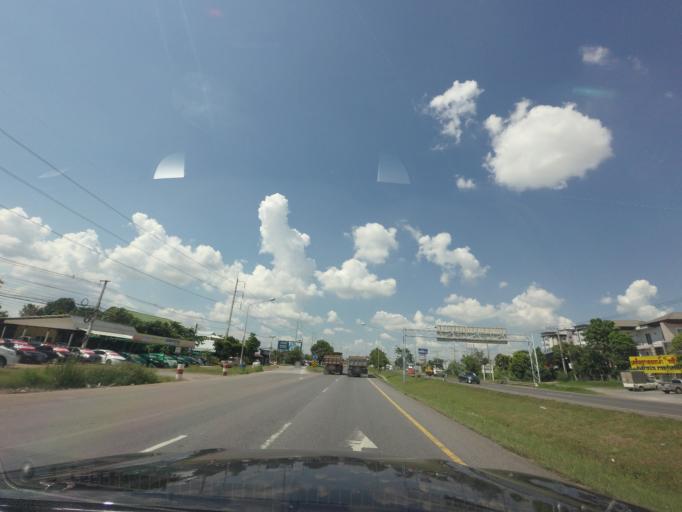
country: TH
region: Nakhon Ratchasima
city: Nakhon Ratchasima
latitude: 14.9724
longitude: 102.0520
